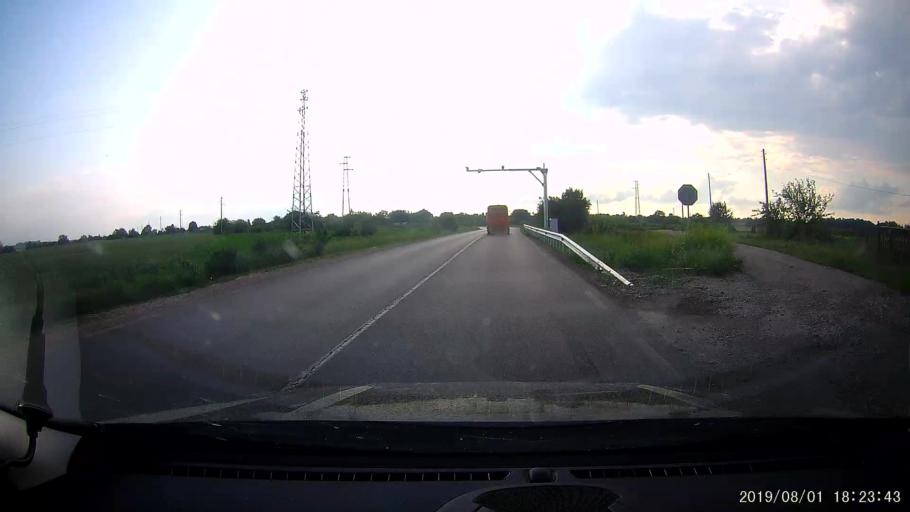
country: BG
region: Shumen
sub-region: Obshtina Kaolinovo
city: Kaolinovo
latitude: 43.6267
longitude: 27.0179
